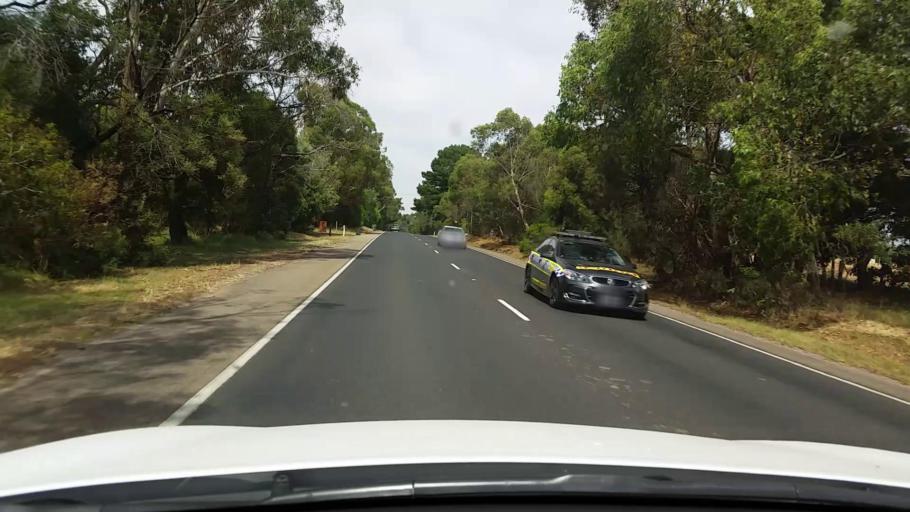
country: AU
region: Victoria
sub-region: Mornington Peninsula
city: Balnarring
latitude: -38.3480
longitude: 145.1635
